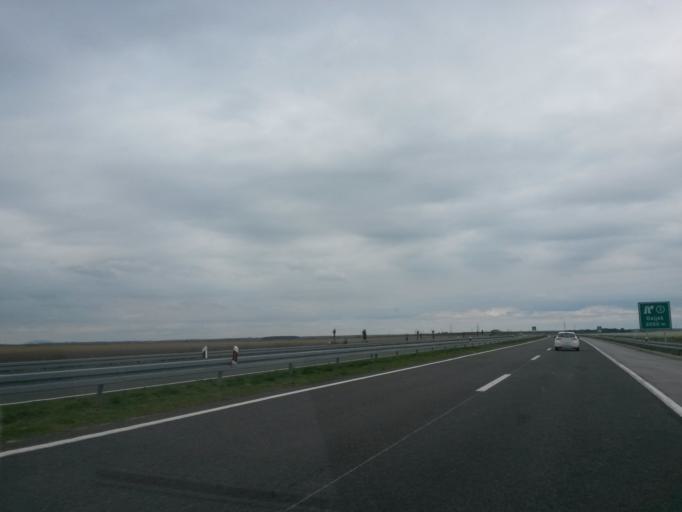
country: HR
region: Osjecko-Baranjska
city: Cepin
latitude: 45.5549
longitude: 18.5411
